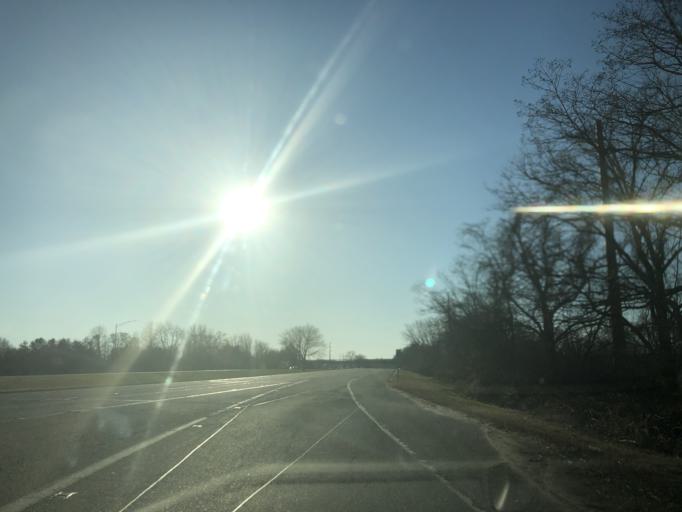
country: US
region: New Jersey
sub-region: Salem County
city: Carneys Point
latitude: 39.7071
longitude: -75.4497
